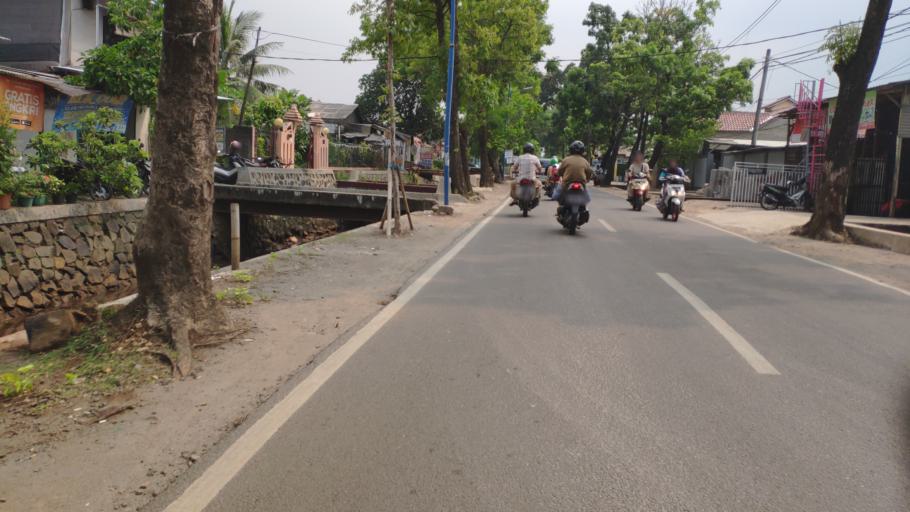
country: ID
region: West Java
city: Depok
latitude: -6.3481
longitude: 106.8135
